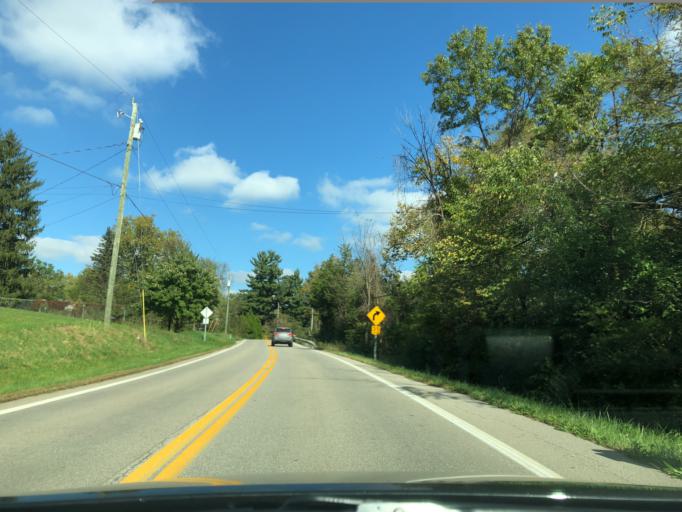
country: US
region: Ohio
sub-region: Hamilton County
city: Loveland
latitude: 39.2782
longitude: -84.2434
